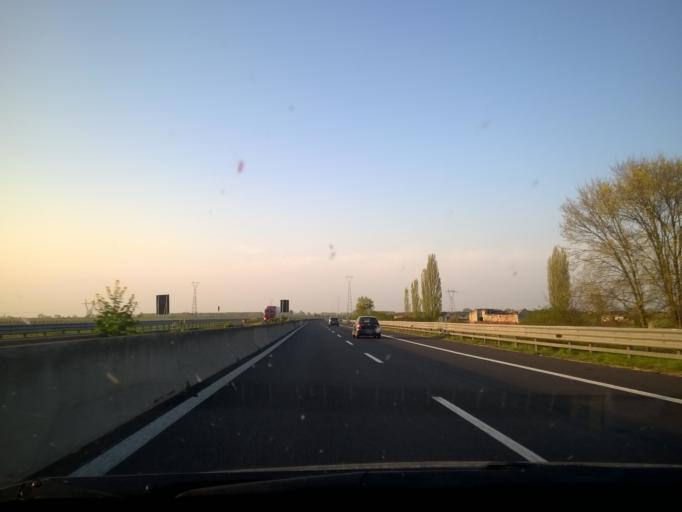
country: IT
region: Veneto
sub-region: Provincia di Rovigo
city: Occhiobello
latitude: 44.9051
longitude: 11.5702
